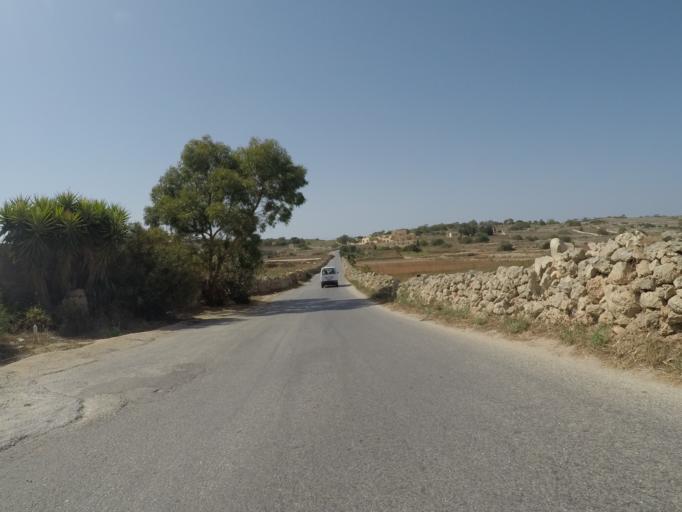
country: MT
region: L-Imgarr
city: Imgarr
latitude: 35.9247
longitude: 14.3792
